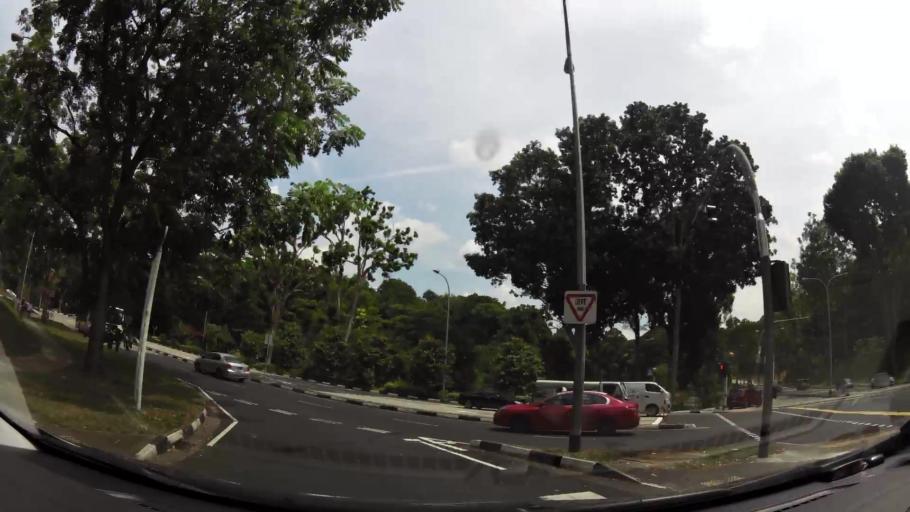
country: SG
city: Singapore
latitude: 1.3469
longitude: 103.7607
